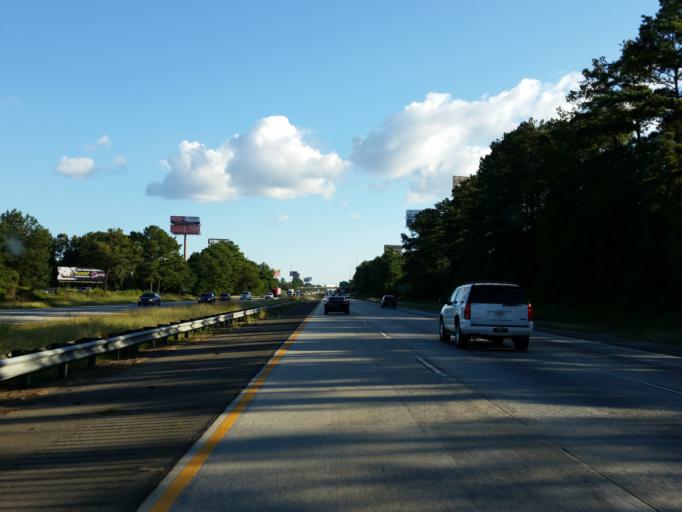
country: US
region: Georgia
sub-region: Peach County
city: Byron
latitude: 32.6210
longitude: -83.7431
